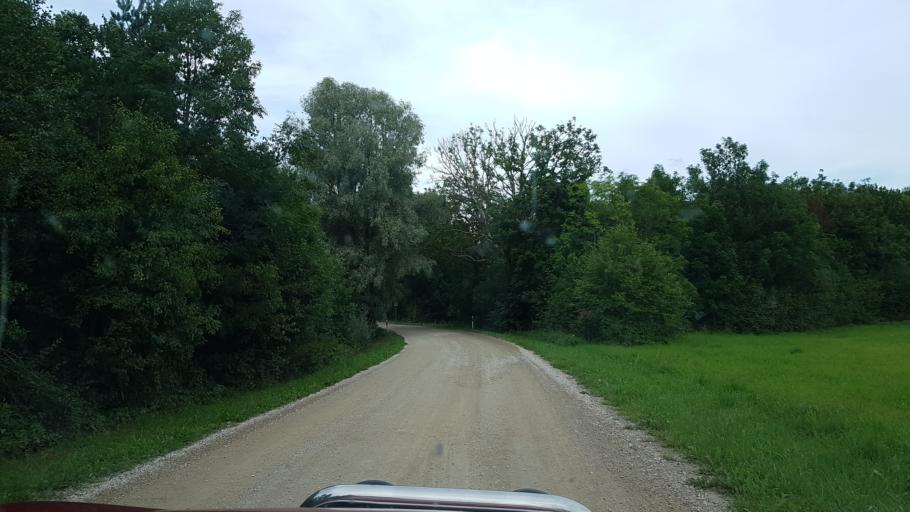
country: EE
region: Laeaene
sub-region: Ridala Parish
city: Uuemoisa
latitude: 59.0189
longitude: 23.7204
